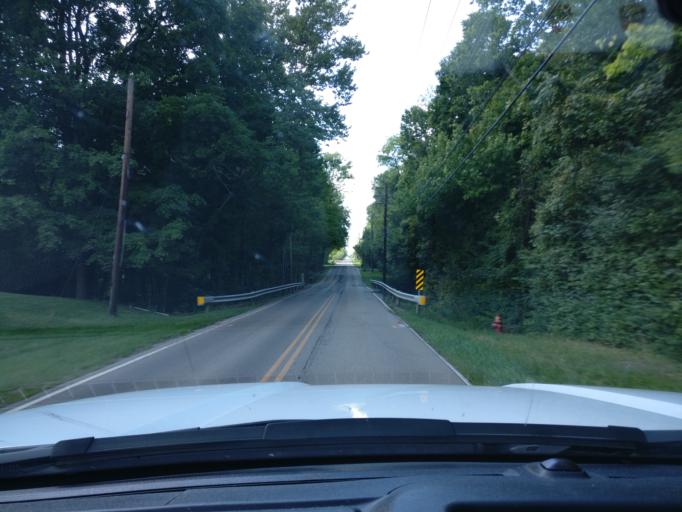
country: US
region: Ohio
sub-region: Warren County
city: Springboro
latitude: 39.5062
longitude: -84.2275
